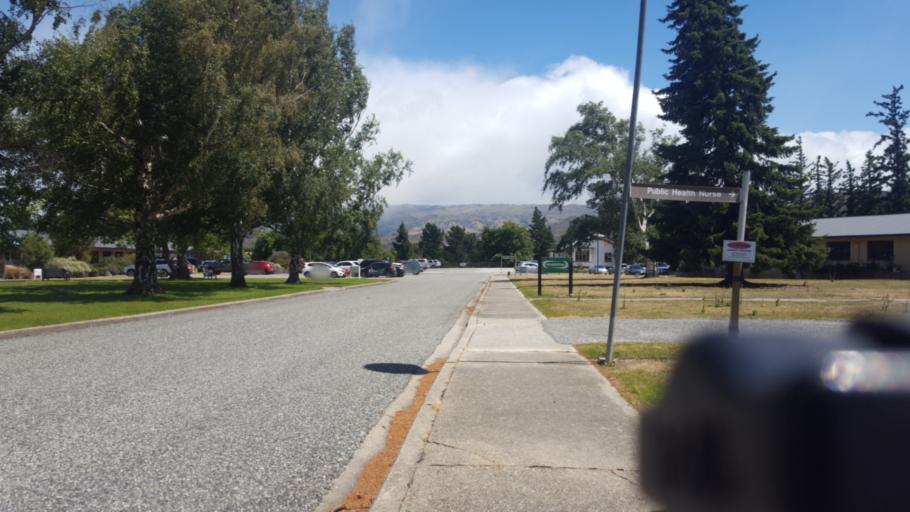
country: NZ
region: Otago
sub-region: Queenstown-Lakes District
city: Wanaka
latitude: -45.2001
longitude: 169.3304
